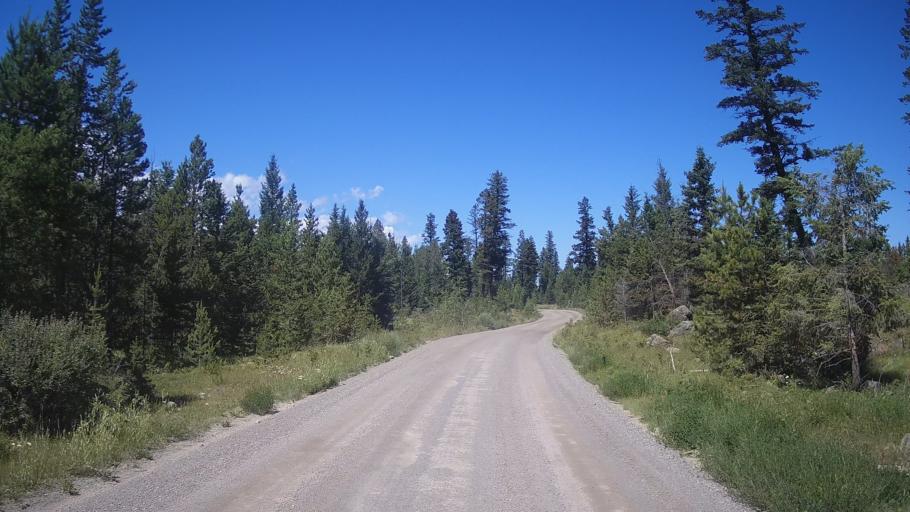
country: CA
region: British Columbia
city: Cache Creek
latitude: 51.1631
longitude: -121.5591
